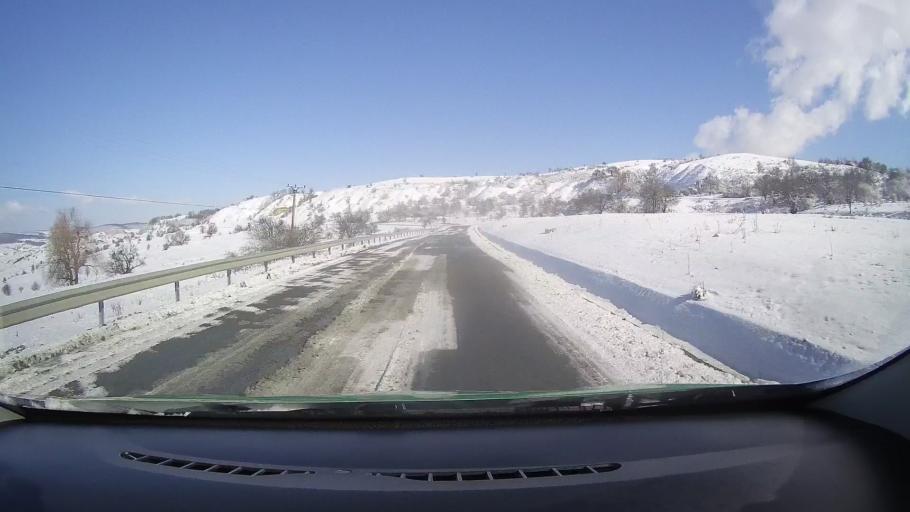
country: RO
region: Sibiu
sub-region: Comuna Avrig
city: Avrig
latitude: 45.7800
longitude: 24.3717
